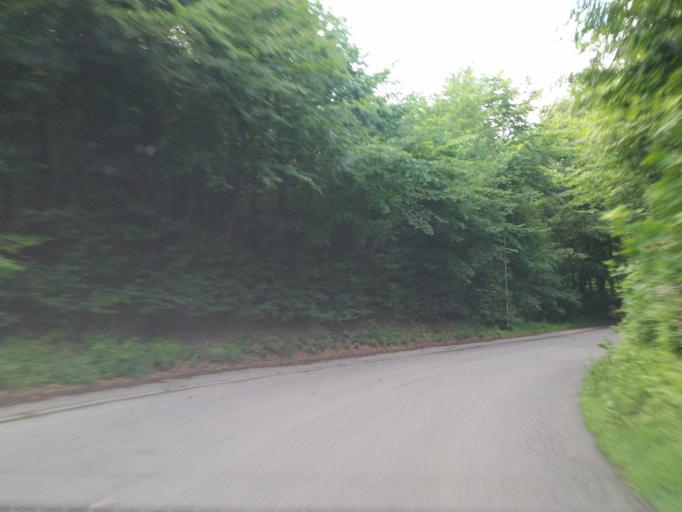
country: DK
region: South Denmark
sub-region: Vejle Kommune
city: Brejning
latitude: 55.6729
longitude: 9.6789
